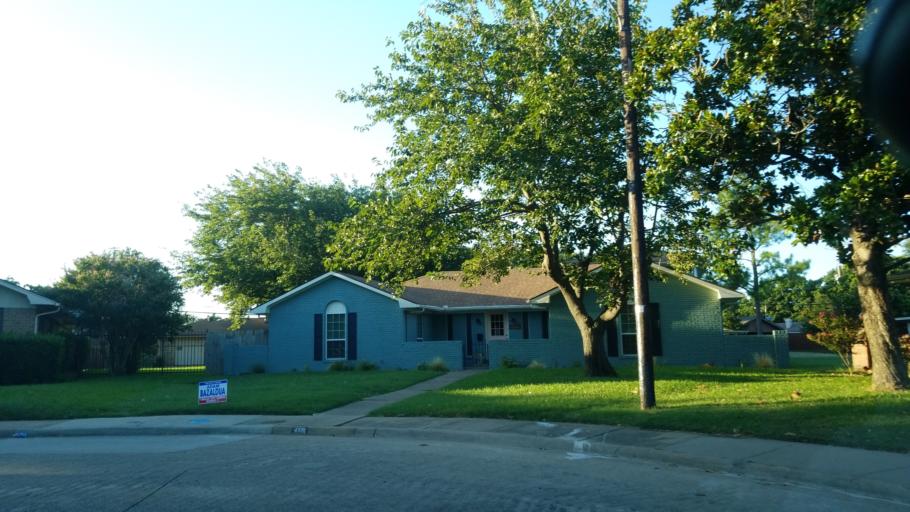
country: US
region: Texas
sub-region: Dallas County
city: Balch Springs
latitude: 32.7890
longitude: -96.6955
